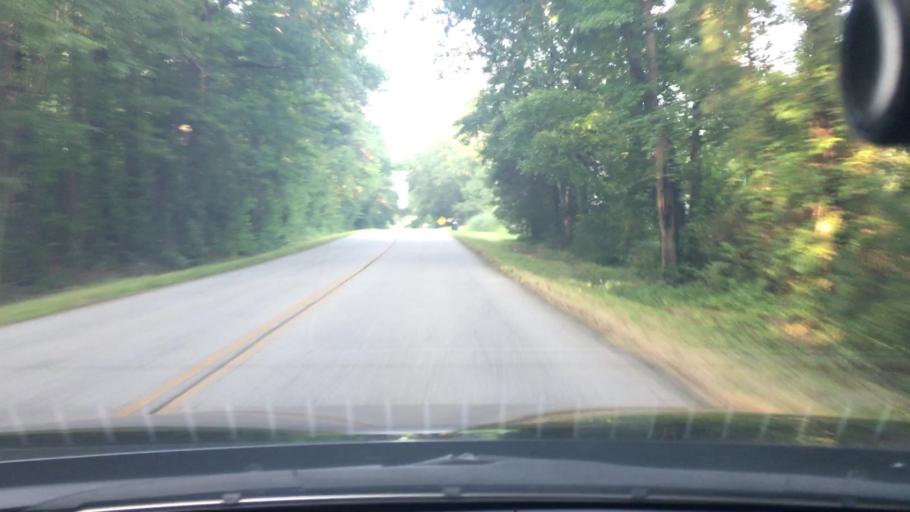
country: US
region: Georgia
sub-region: Fayette County
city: Peachtree City
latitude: 33.3947
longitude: -84.6240
